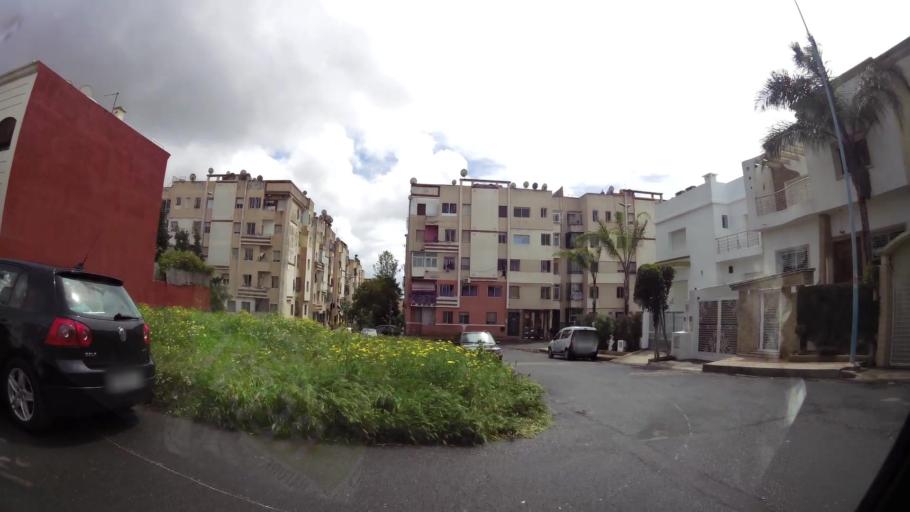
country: MA
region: Grand Casablanca
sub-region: Casablanca
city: Casablanca
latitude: 33.5282
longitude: -7.6451
